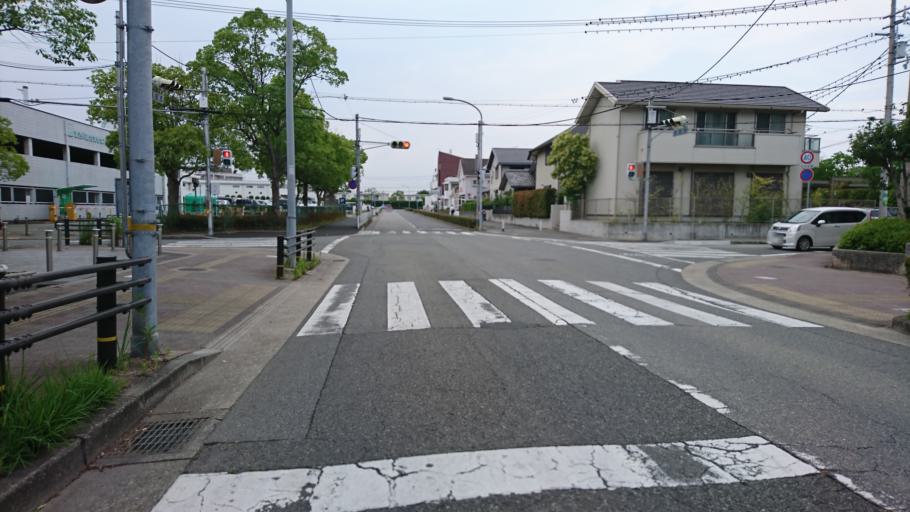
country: JP
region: Hyogo
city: Kakogawacho-honmachi
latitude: 34.7500
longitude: 134.8731
